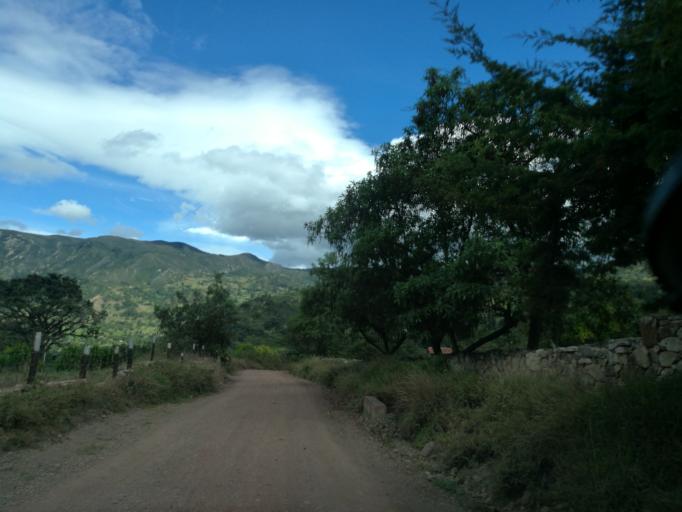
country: CO
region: Boyaca
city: Socota
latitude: 6.1190
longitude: -72.7145
